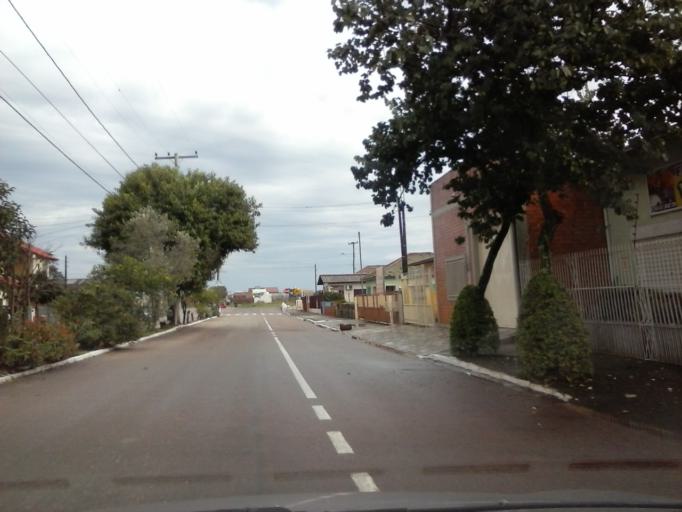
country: BR
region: Rio Grande do Sul
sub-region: Porto Alegre
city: Porto Alegre
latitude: -30.0002
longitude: -51.3108
